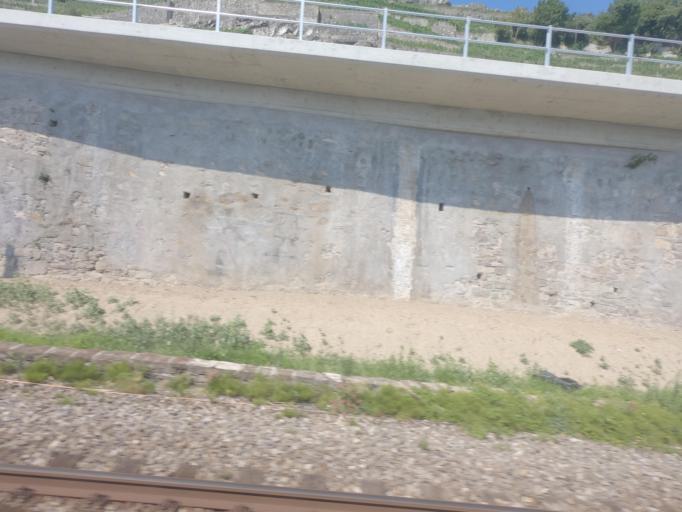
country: CH
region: Vaud
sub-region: Lavaux-Oron District
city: Chexbres
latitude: 46.4766
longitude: 6.7712
